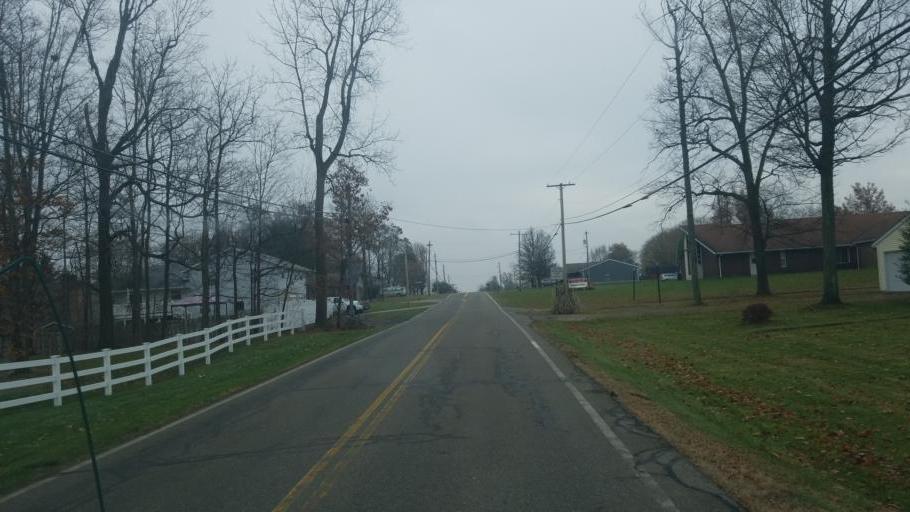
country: US
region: Ohio
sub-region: Richland County
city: Lexington
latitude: 40.7106
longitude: -82.5411
